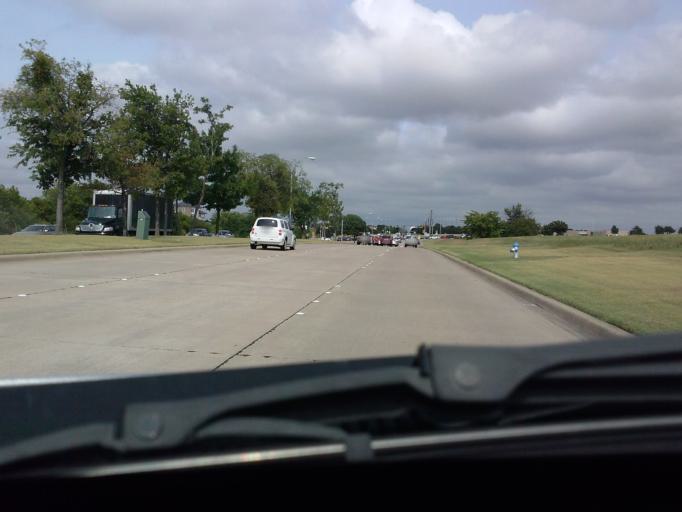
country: US
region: Texas
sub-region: Denton County
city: The Colony
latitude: 33.0565
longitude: -96.7983
